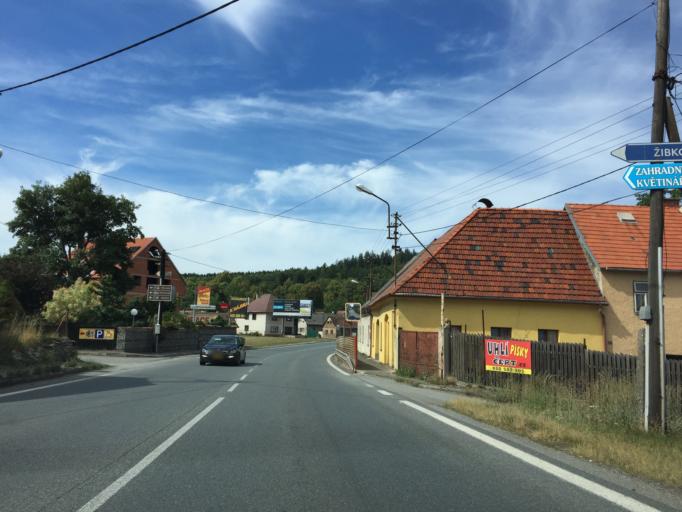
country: CZ
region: Central Bohemia
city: Votice
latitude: 49.5700
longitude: 14.6590
